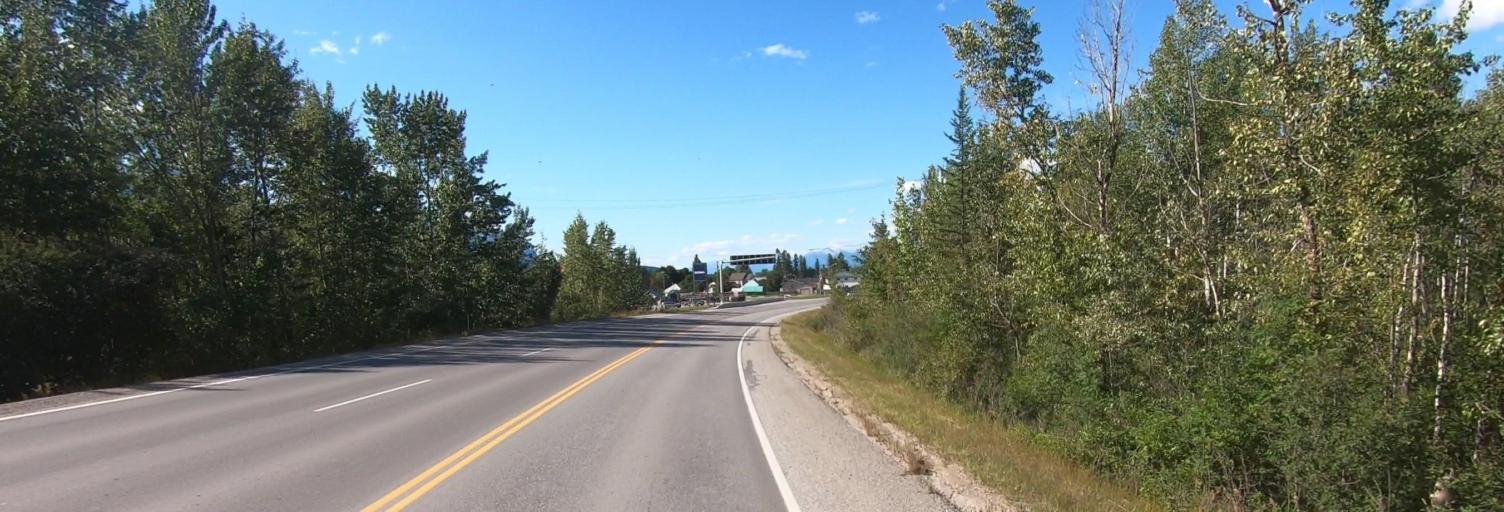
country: CA
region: British Columbia
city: Golden
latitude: 51.2892
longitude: -116.9618
